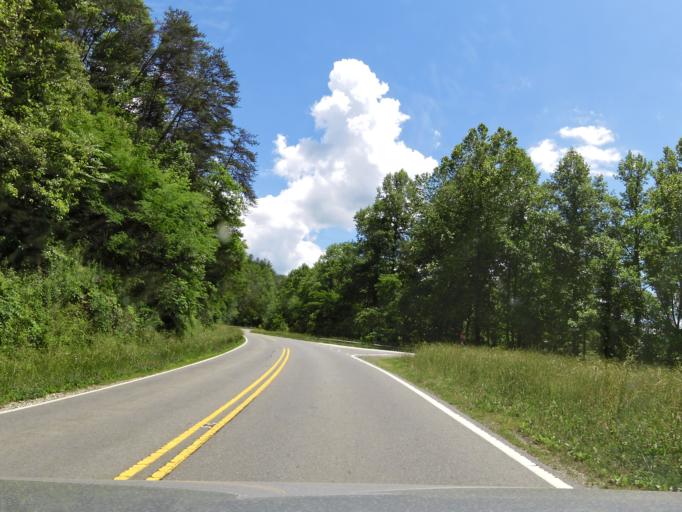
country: US
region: North Carolina
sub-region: Graham County
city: Robbinsville
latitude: 35.3491
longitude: -83.8303
